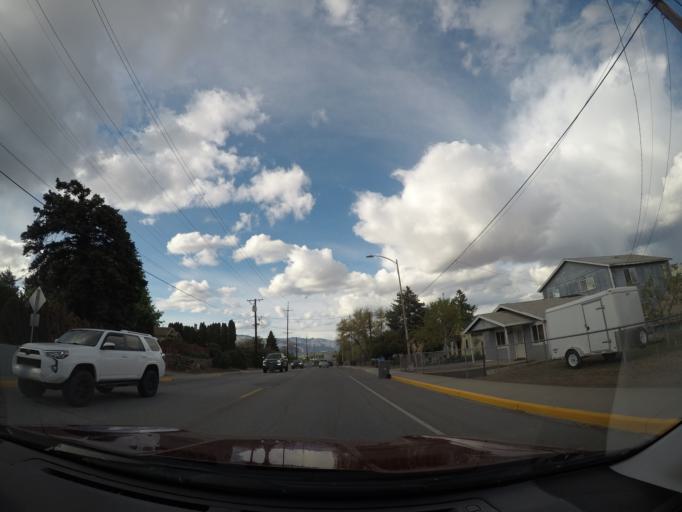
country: US
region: Washington
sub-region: Douglas County
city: East Wenatchee
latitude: 47.4052
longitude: -120.3031
